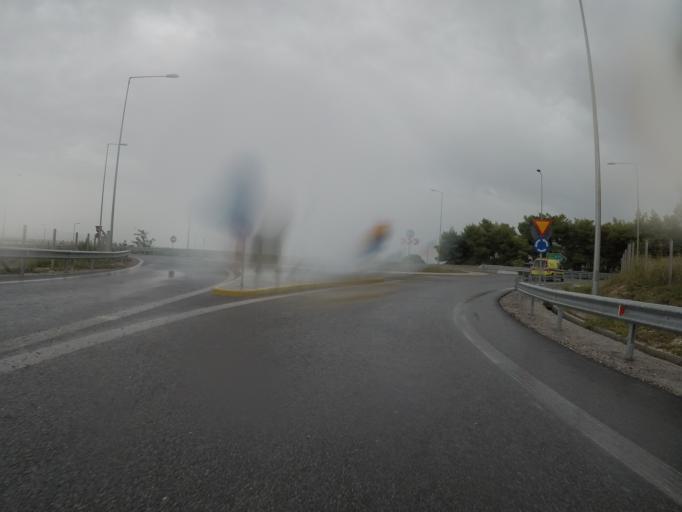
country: GR
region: Peloponnese
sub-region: Nomos Korinthias
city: Arkhaia Korinthos
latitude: 37.9137
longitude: 22.8855
